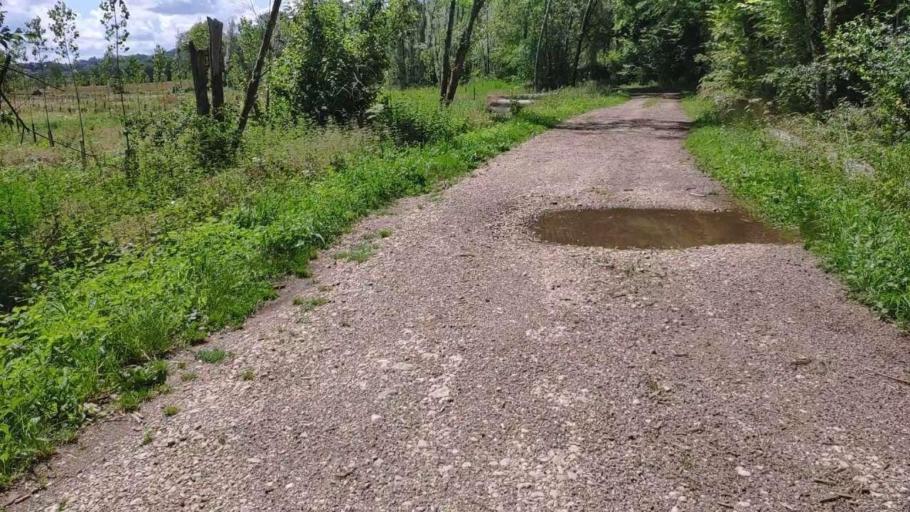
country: FR
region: Franche-Comte
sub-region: Departement du Jura
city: Poligny
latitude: 46.8197
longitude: 5.5730
